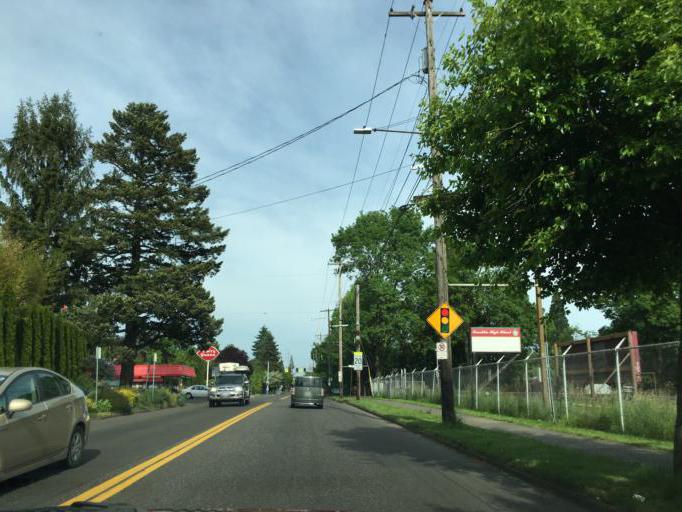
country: US
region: Oregon
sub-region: Multnomah County
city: Lents
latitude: 45.5053
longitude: -122.6067
